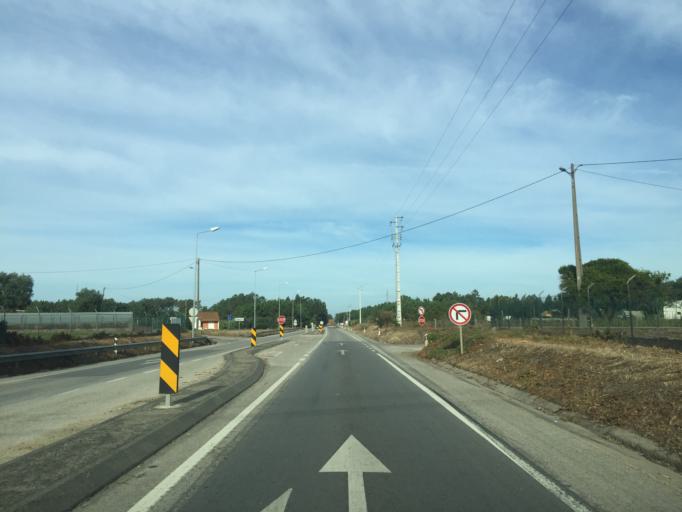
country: PT
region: Coimbra
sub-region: Figueira da Foz
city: Lavos
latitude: 40.0250
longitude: -8.8222
